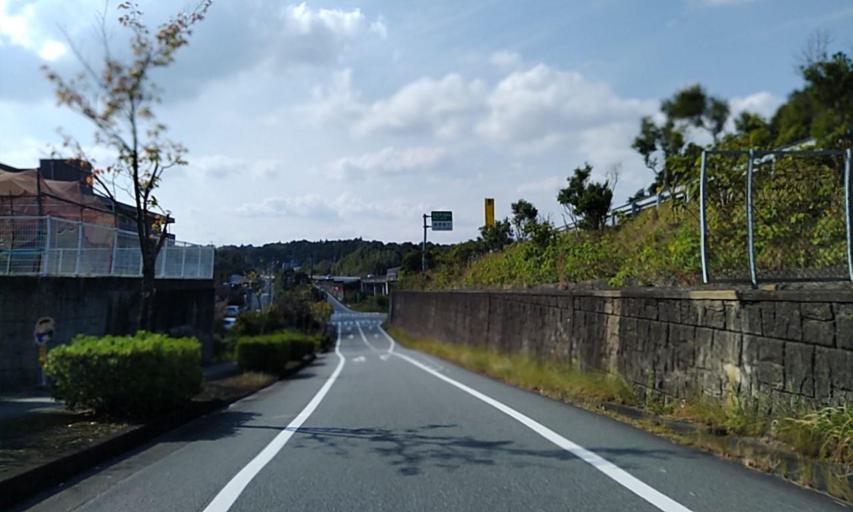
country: JP
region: Mie
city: Ise
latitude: 34.4737
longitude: 136.7138
